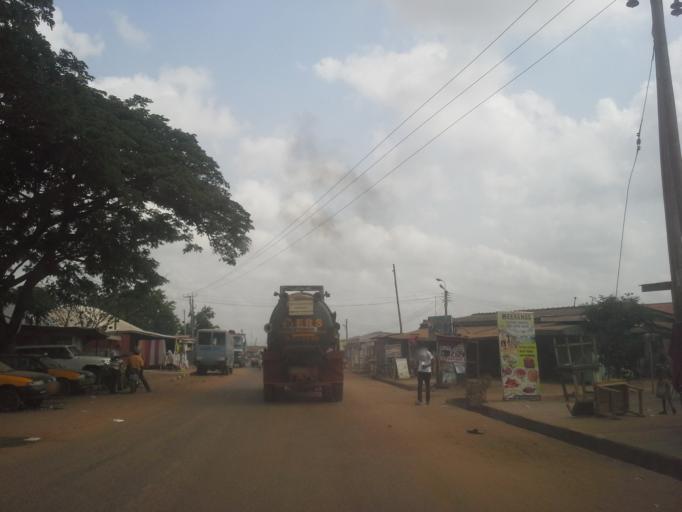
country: GH
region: Greater Accra
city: Tema
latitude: 5.6860
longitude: -0.0393
